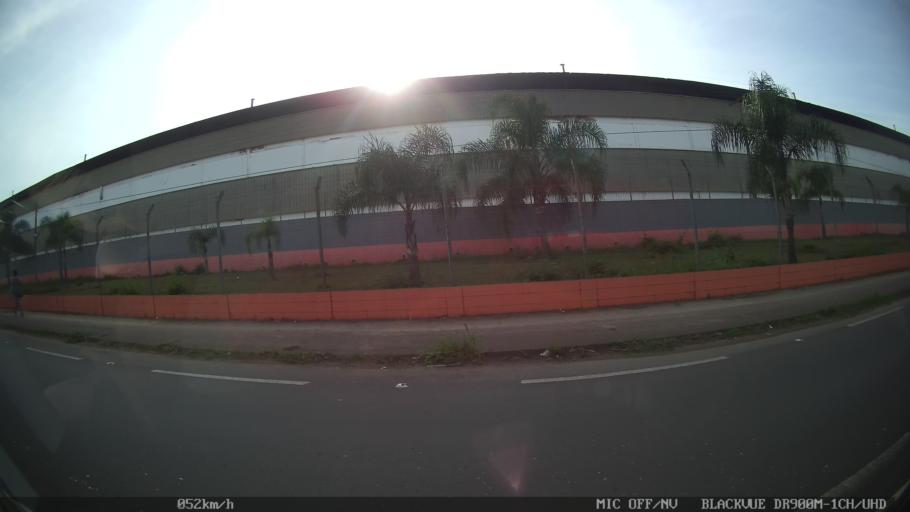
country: BR
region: Sao Paulo
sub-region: Piracicaba
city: Piracicaba
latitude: -22.6994
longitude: -47.6592
